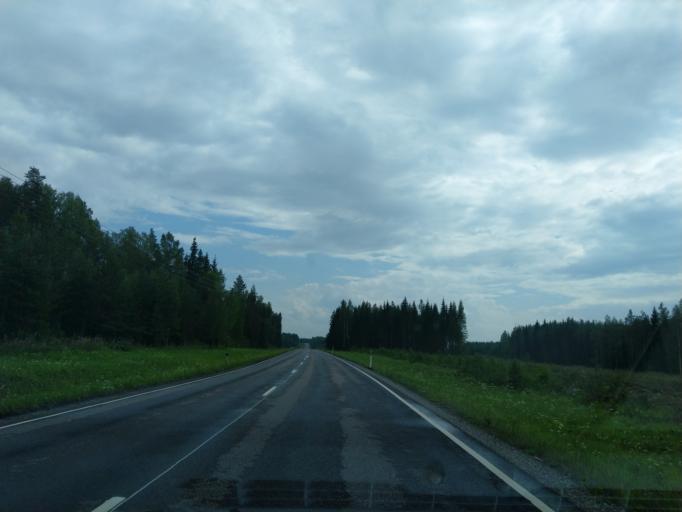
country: FI
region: South Karelia
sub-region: Imatra
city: Parikkala
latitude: 61.6270
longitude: 29.4340
